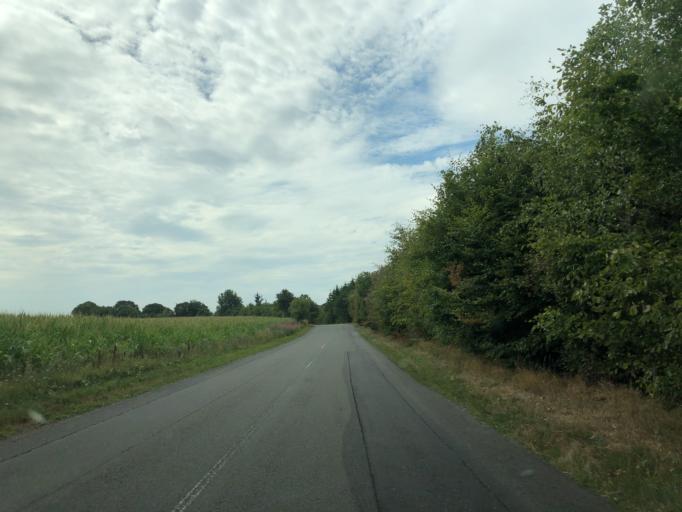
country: DK
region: South Denmark
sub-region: Vejle Kommune
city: Egtved
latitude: 55.6394
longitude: 9.1996
